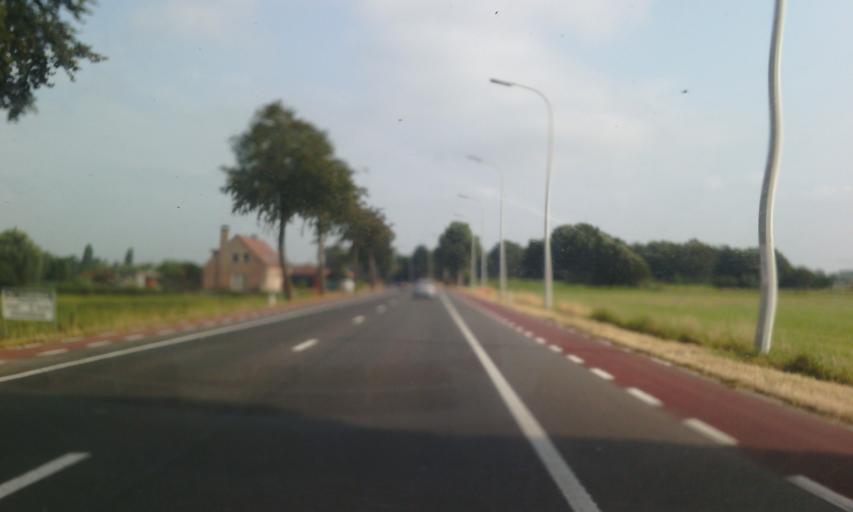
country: BE
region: Flanders
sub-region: Provincie Oost-Vlaanderen
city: Waarschoot
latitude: 51.1612
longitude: 3.5892
